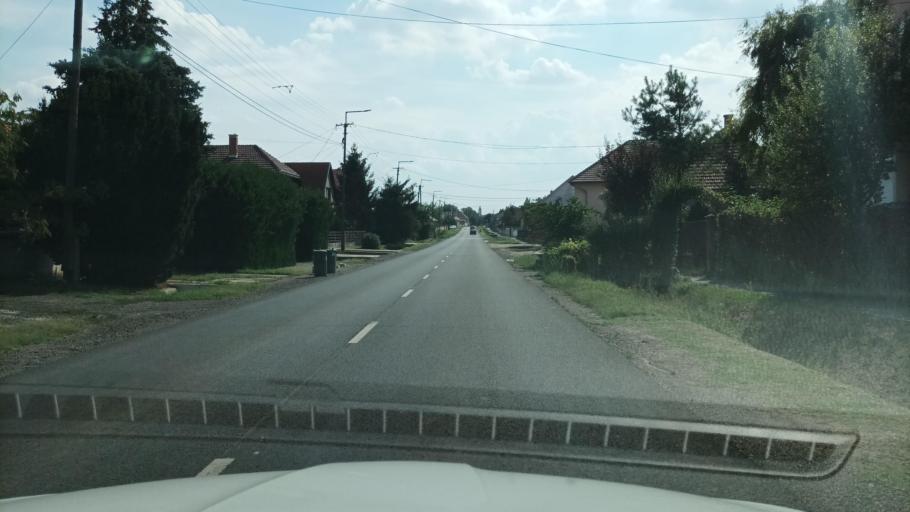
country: HU
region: Pest
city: Zsambok
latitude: 47.5544
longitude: 19.6048
